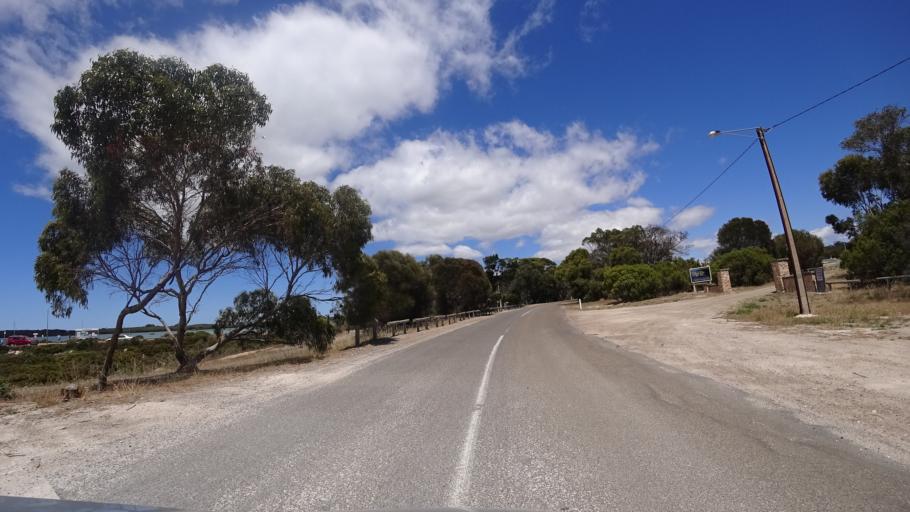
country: AU
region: South Australia
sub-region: Kangaroo Island
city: Kingscote
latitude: -35.7867
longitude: 137.7722
